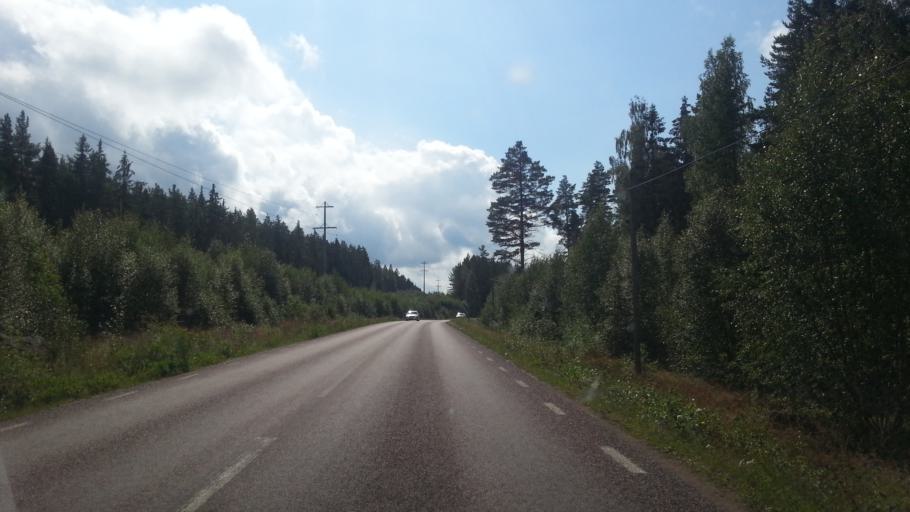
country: SE
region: Dalarna
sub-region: Faluns Kommun
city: Svardsjo
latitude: 60.6505
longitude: 15.7858
